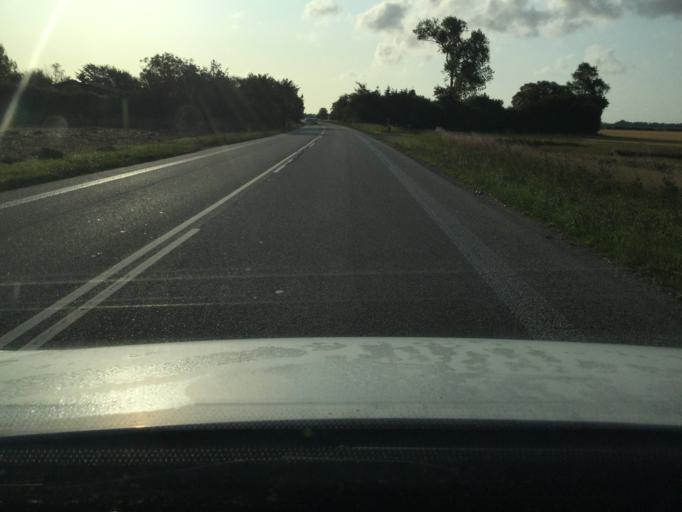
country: DK
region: Zealand
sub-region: Lolland Kommune
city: Rodby
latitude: 54.7656
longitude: 11.3076
